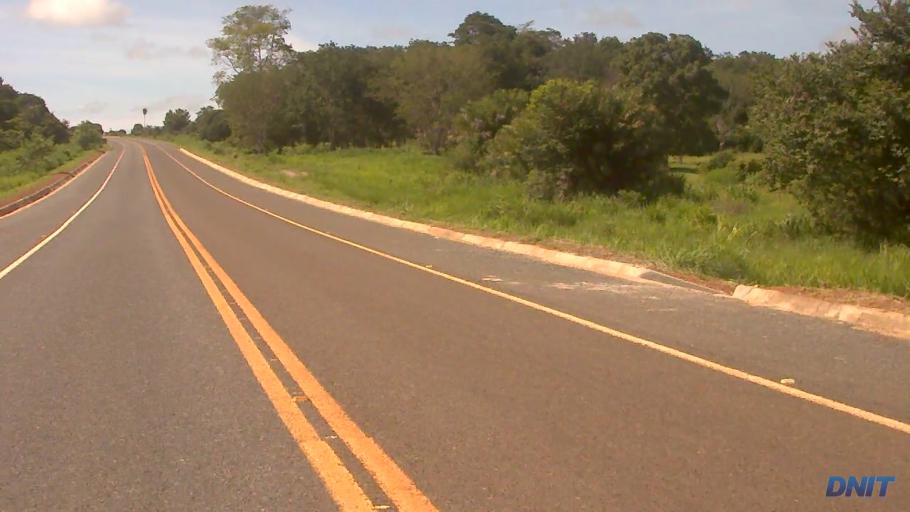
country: BR
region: Goias
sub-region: Sao Miguel Do Araguaia
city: Sao Miguel do Araguaia
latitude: -13.2921
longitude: -50.1774
